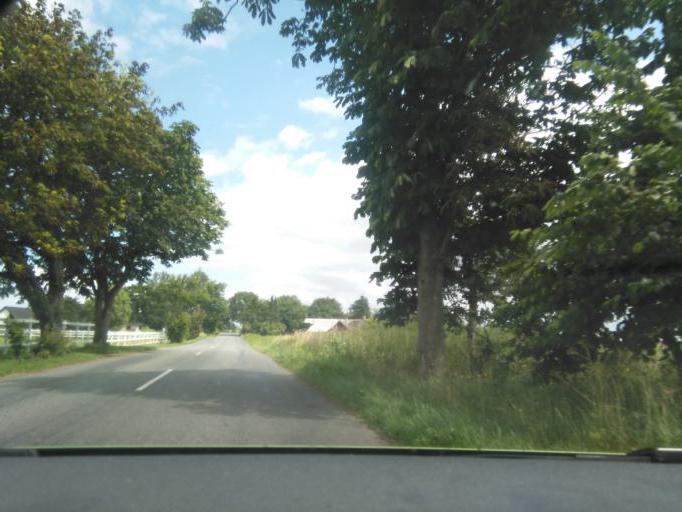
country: DK
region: Zealand
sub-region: Kalundborg Kommune
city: Gorlev
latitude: 55.5474
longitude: 11.1784
